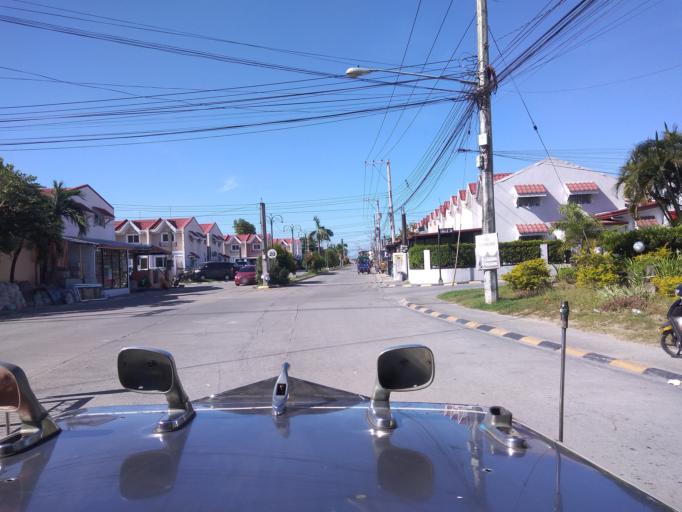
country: PH
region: Central Luzon
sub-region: Province of Pampanga
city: Calibutbut
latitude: 15.0998
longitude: 120.6026
